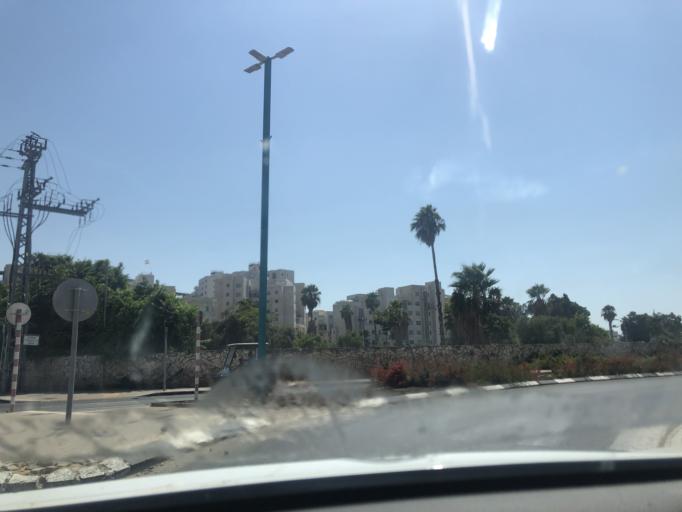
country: IL
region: Central District
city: Lod
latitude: 31.9570
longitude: 34.8956
